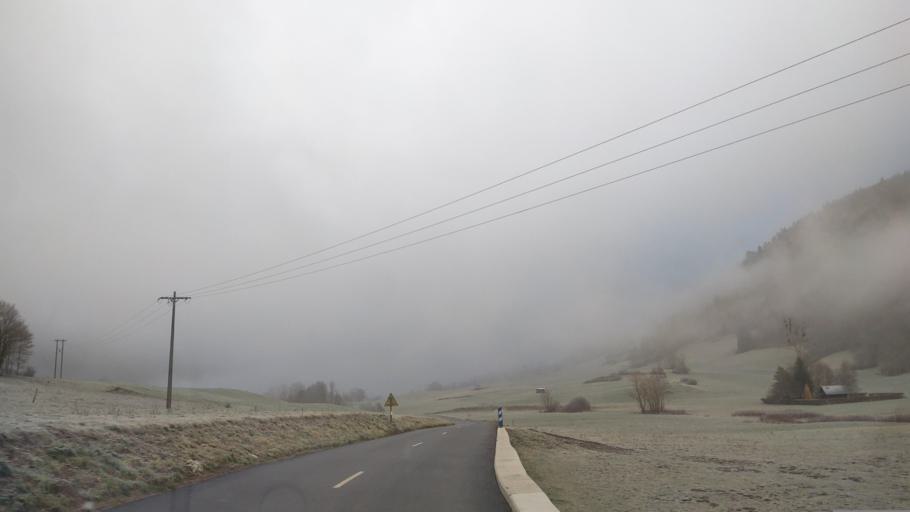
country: FR
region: Rhone-Alpes
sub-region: Departement de la Savoie
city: Coise-Saint-Jean-Pied-Gauthier
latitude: 45.6075
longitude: 6.1411
